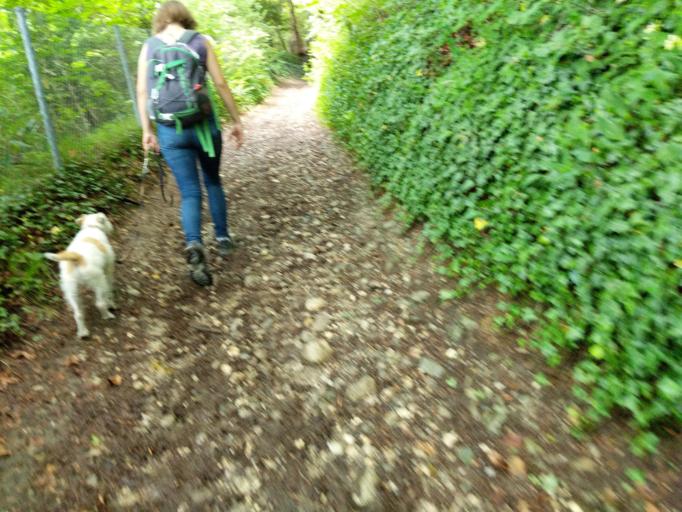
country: DE
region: Bavaria
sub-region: Upper Bavaria
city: Herrsching am Ammersee
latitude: 48.0049
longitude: 11.1851
